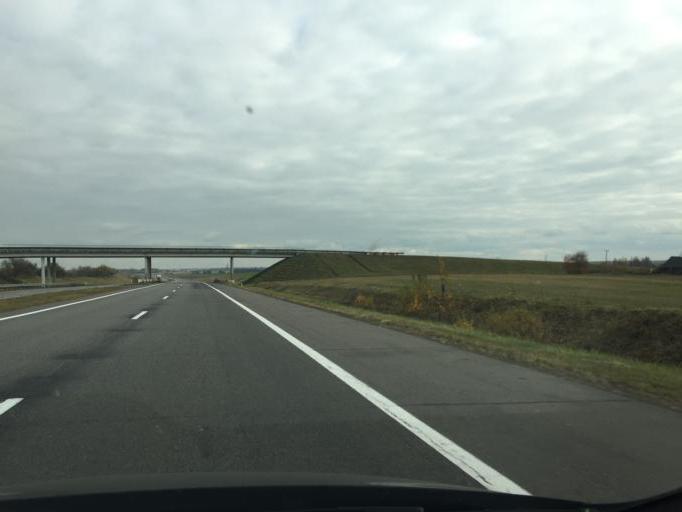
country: BY
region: Minsk
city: Stan'kava
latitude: 53.6768
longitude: 27.2067
